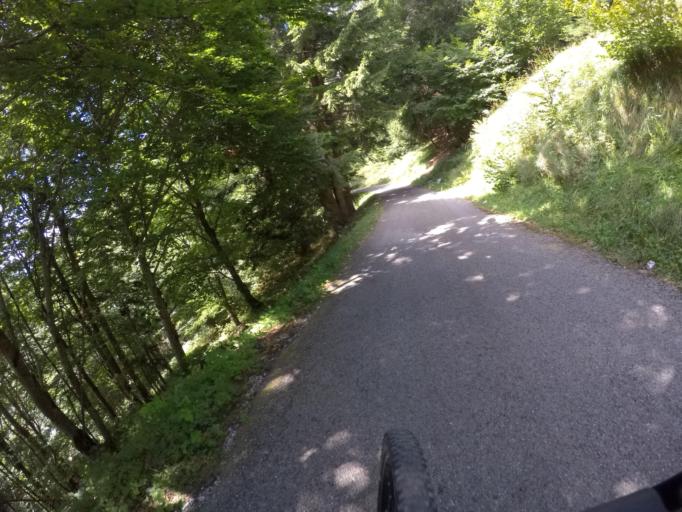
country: IT
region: Friuli Venezia Giulia
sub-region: Provincia di Udine
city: Ligosullo
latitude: 46.4986
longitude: 13.0688
